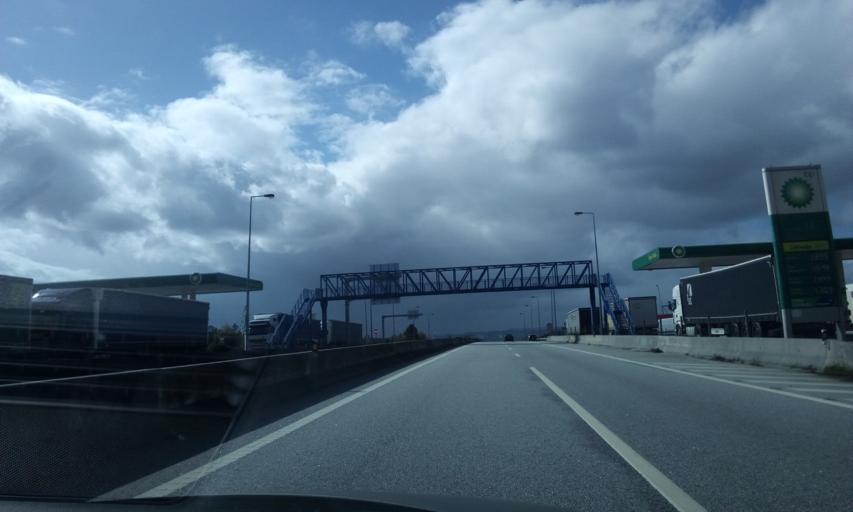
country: PT
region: Viseu
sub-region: Mangualde
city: Mangualde
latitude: 40.6254
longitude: -7.7803
